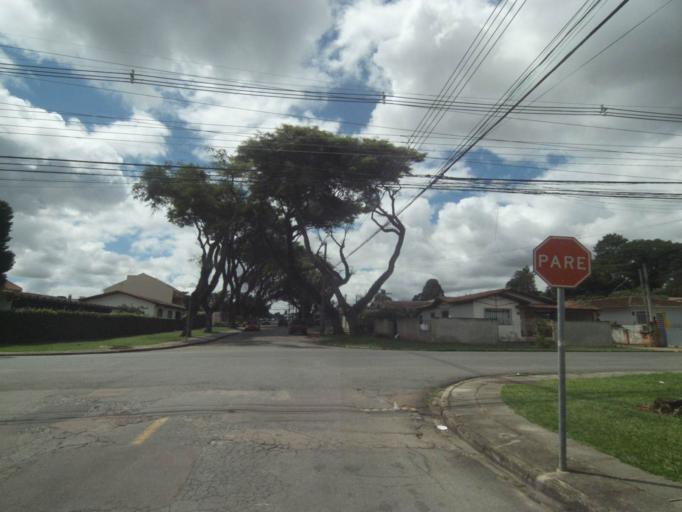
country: BR
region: Parana
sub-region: Curitiba
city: Curitiba
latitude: -25.4814
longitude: -49.2677
